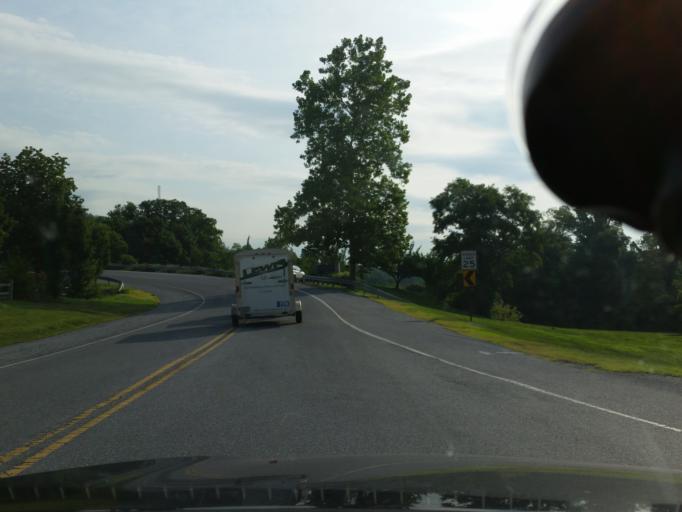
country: US
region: Pennsylvania
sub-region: Cumberland County
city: Enola
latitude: 40.3123
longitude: -76.9295
